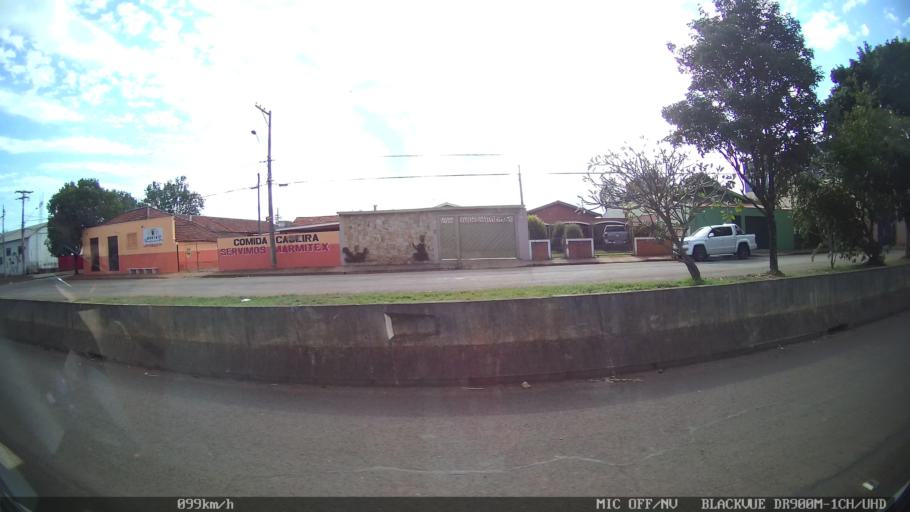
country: BR
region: Sao Paulo
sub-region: Iracemapolis
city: Iracemapolis
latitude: -22.5926
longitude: -47.4644
